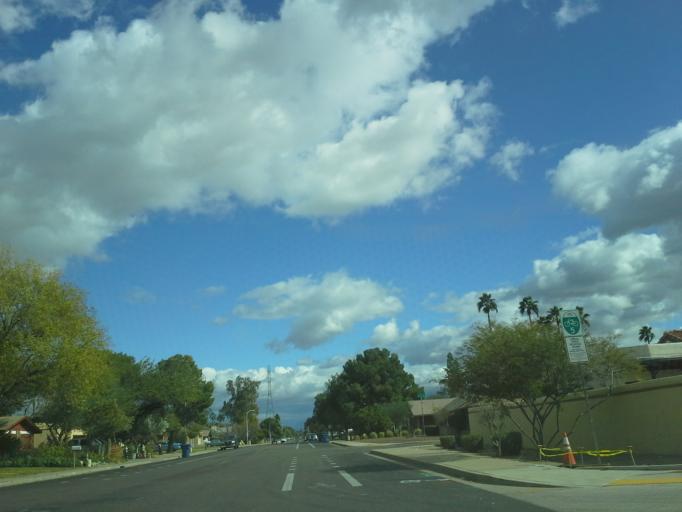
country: US
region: Arizona
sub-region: Maricopa County
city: Mesa
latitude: 33.4442
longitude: -111.8046
